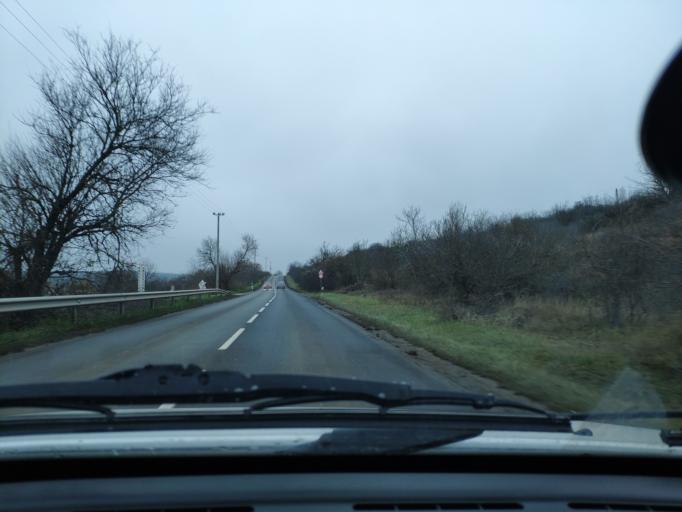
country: HU
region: Pest
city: Soskut
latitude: 47.4133
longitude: 18.8296
